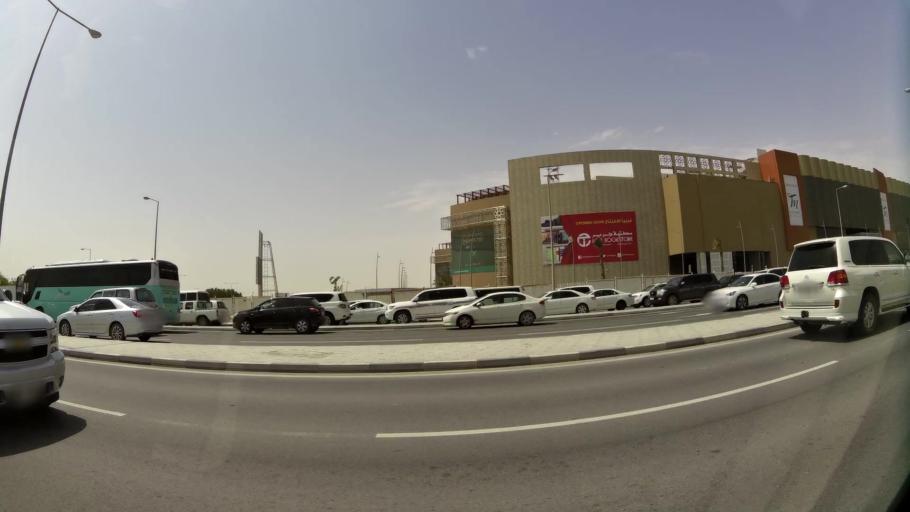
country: QA
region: Baladiyat ad Dawhah
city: Doha
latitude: 25.3360
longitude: 51.4821
